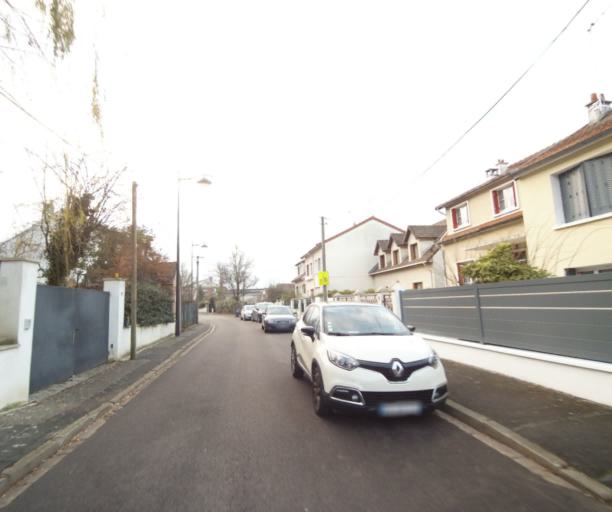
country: FR
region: Ile-de-France
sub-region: Departement des Hauts-de-Seine
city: Rueil-Malmaison
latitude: 48.8748
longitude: 2.2058
